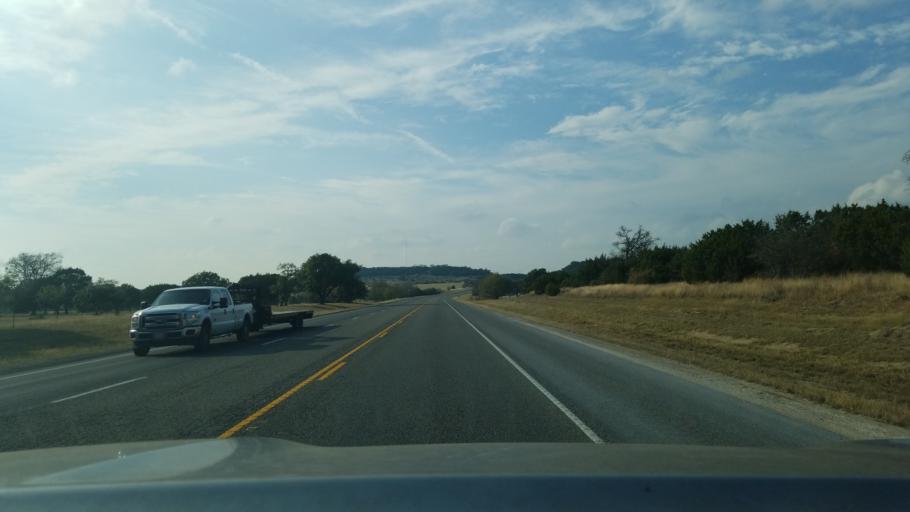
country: US
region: Texas
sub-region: Lampasas County
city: Lampasas
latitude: 31.1362
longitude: -98.3035
